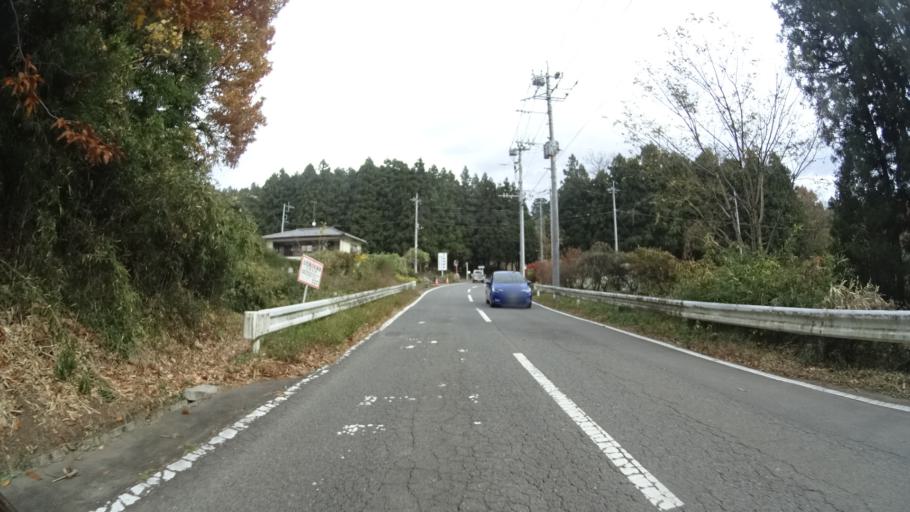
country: JP
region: Gunma
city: Maebashi-shi
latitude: 36.4736
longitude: 139.1400
